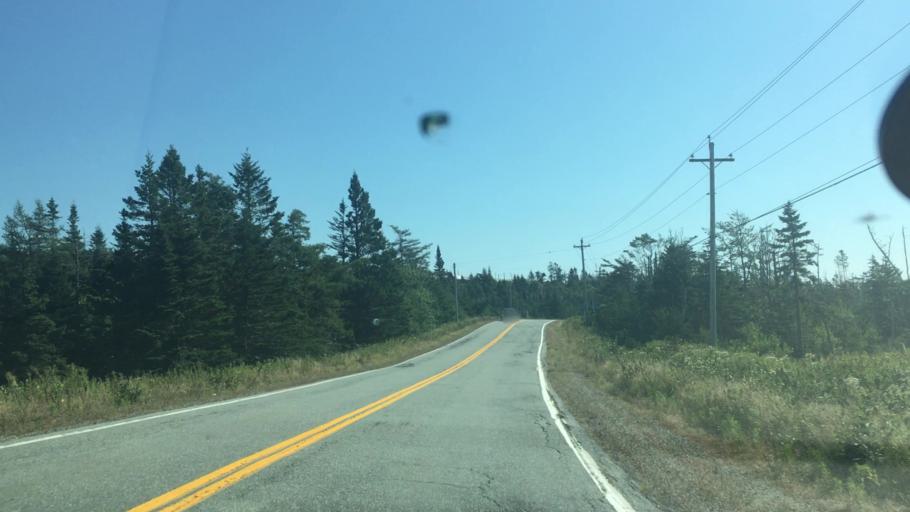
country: CA
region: Nova Scotia
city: New Glasgow
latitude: 44.9175
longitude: -62.3228
